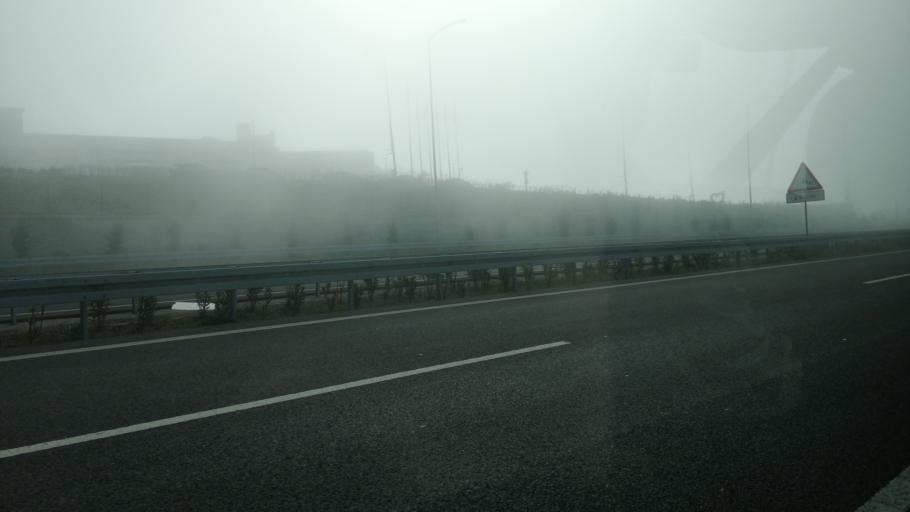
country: TR
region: Kocaeli
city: Tavsanli
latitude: 40.7726
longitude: 29.5183
